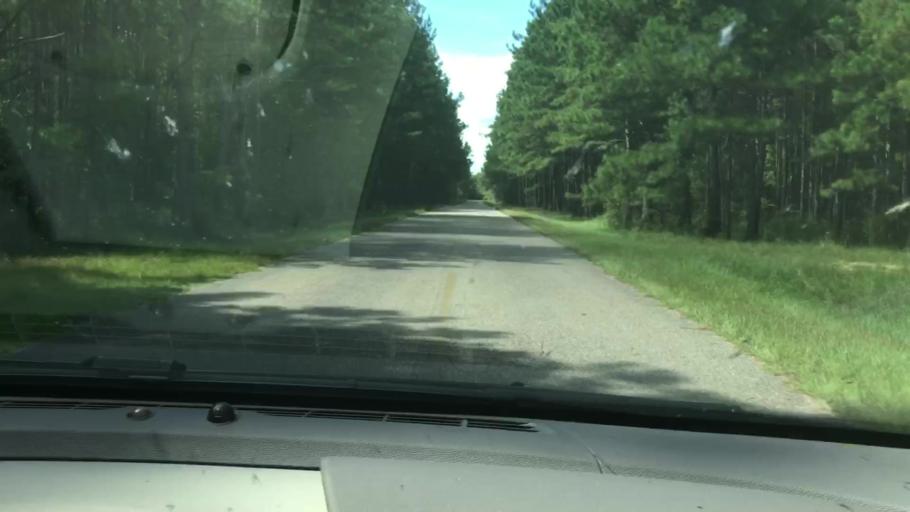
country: US
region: Georgia
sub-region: Clay County
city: Fort Gaines
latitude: 31.7421
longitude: -85.0765
